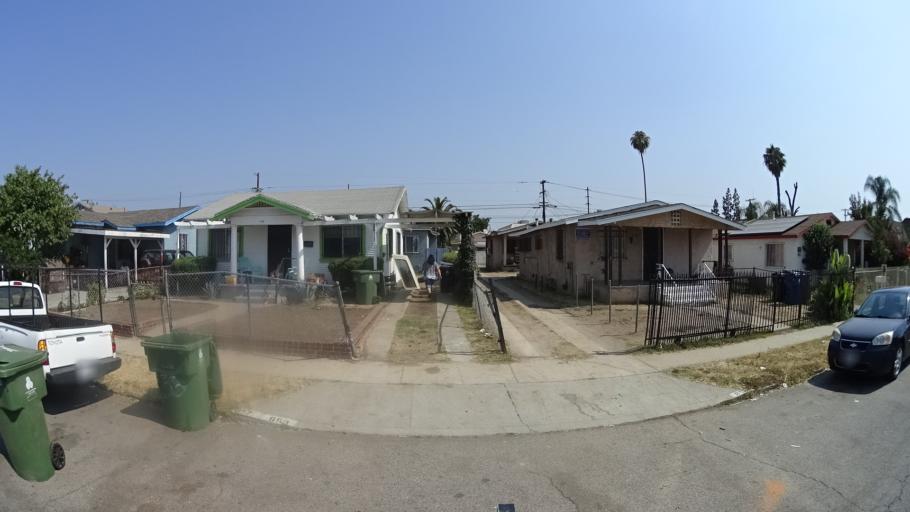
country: US
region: California
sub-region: Los Angeles County
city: Westmont
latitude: 33.9678
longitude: -118.2889
